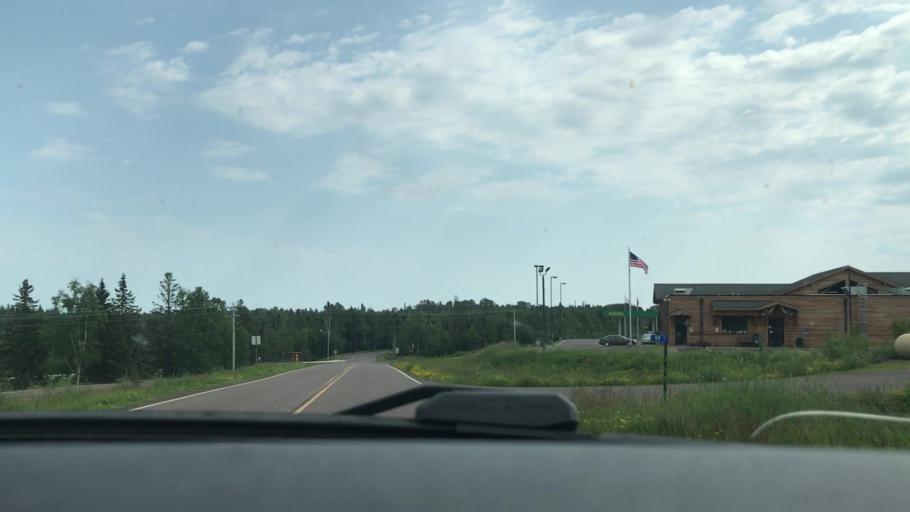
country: CA
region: Ontario
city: Neebing
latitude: 47.9549
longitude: -89.6941
